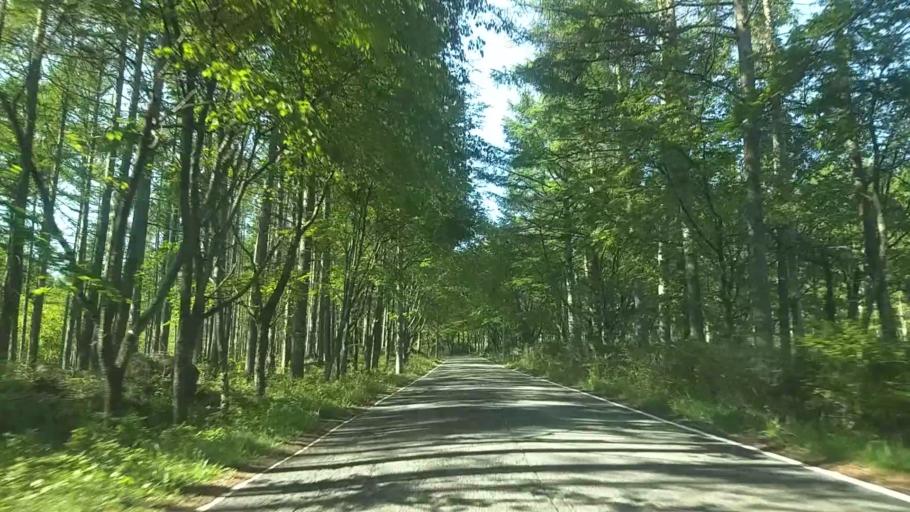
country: JP
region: Nagano
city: Chino
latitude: 35.8979
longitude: 138.3506
